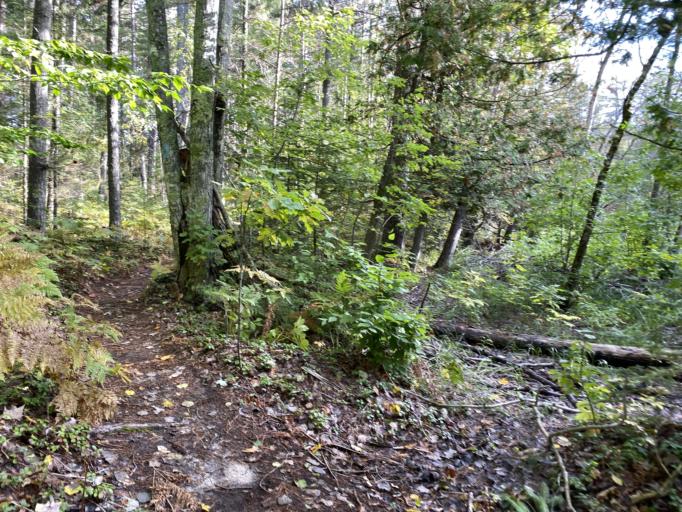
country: US
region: Michigan
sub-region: Mackinac County
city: Saint Ignace
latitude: 45.7426
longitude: -84.8845
